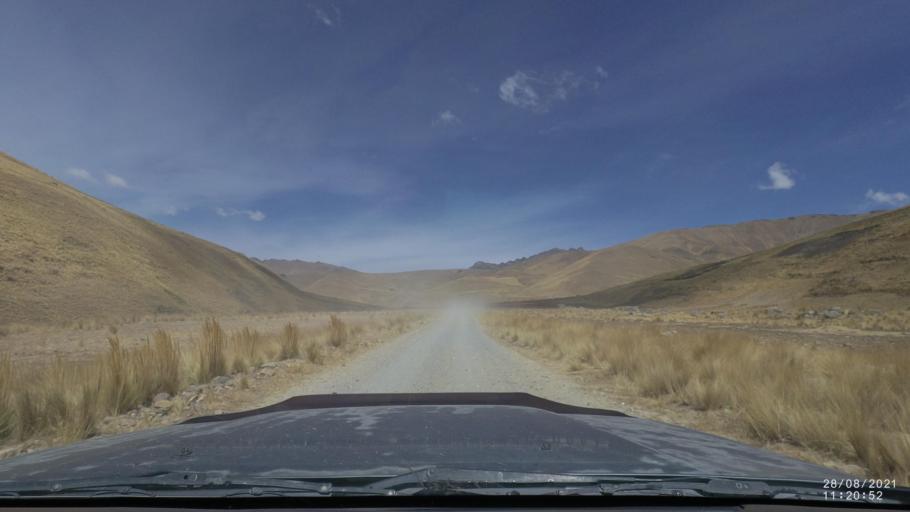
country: BO
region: Cochabamba
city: Sipe Sipe
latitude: -17.1614
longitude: -66.3435
